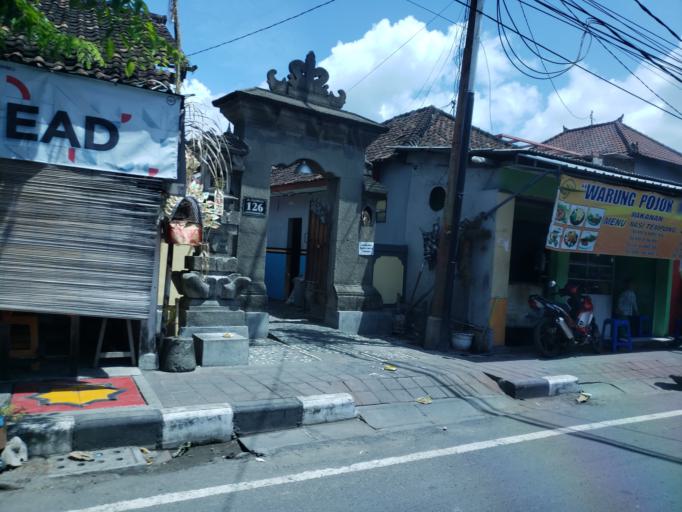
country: ID
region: Bali
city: Kelanabian
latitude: -8.7544
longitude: 115.1776
